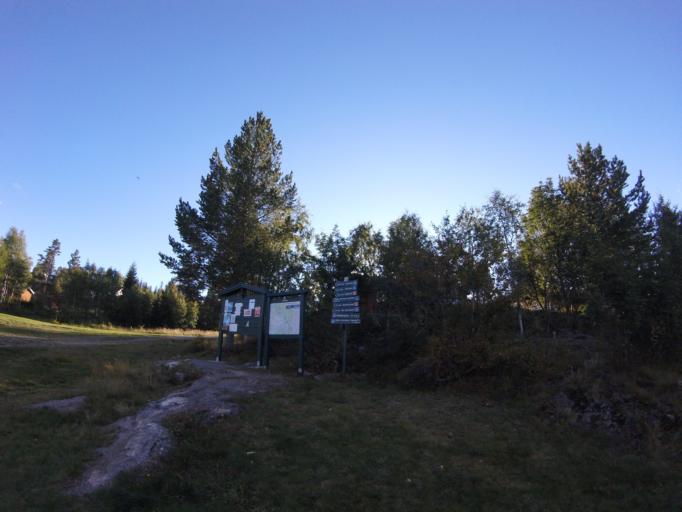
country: NO
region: Buskerud
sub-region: Flesberg
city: Lampeland
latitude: 59.7899
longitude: 9.4146
